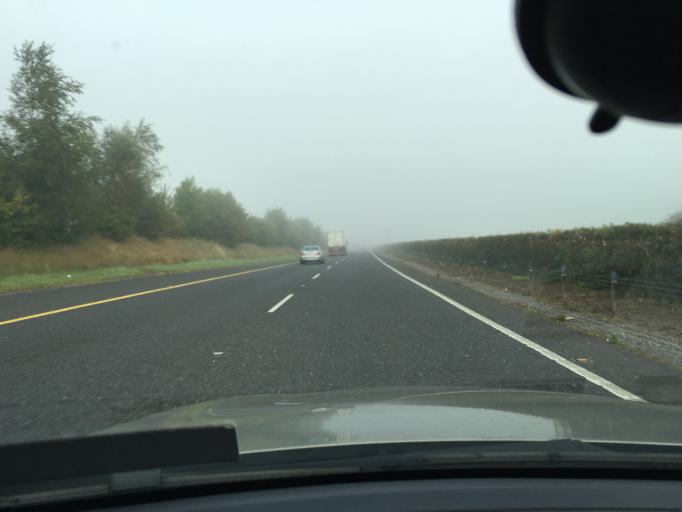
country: IE
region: Leinster
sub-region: An Mhi
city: Longwood
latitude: 53.4149
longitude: -6.9028
